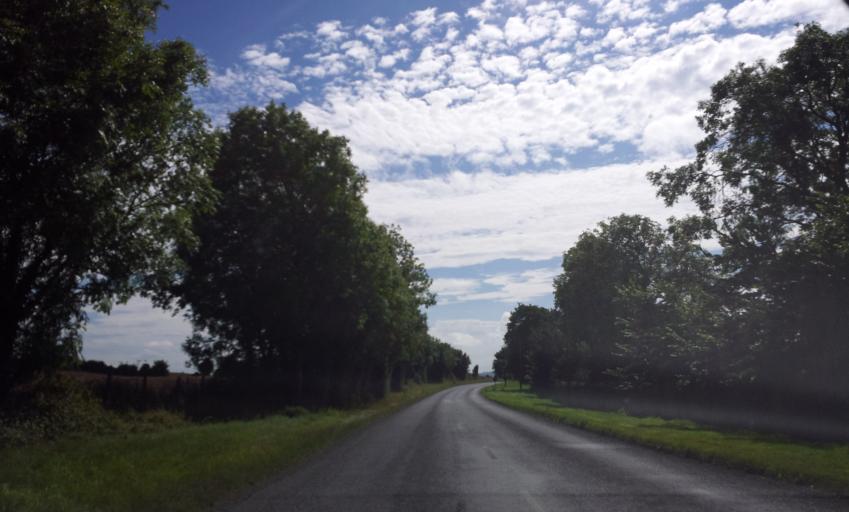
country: IE
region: Leinster
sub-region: Laois
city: Portlaoise
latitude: 53.0063
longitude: -7.2307
